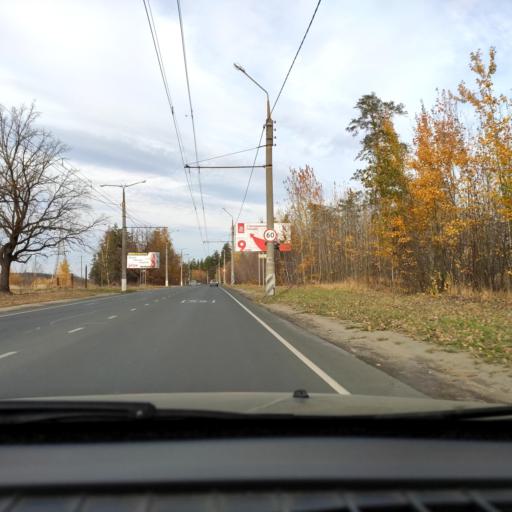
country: RU
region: Samara
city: Tol'yatti
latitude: 53.4873
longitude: 49.3826
